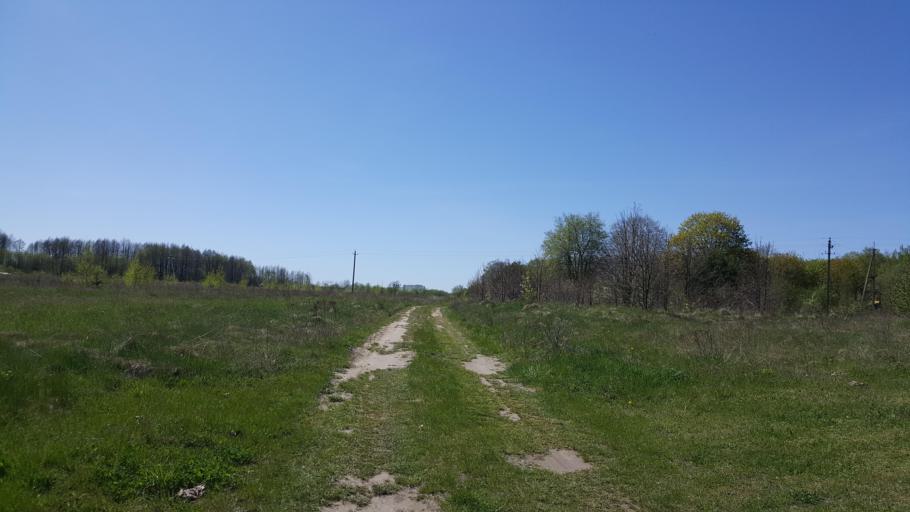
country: BY
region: Brest
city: Kamyanyets
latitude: 52.4543
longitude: 23.8737
